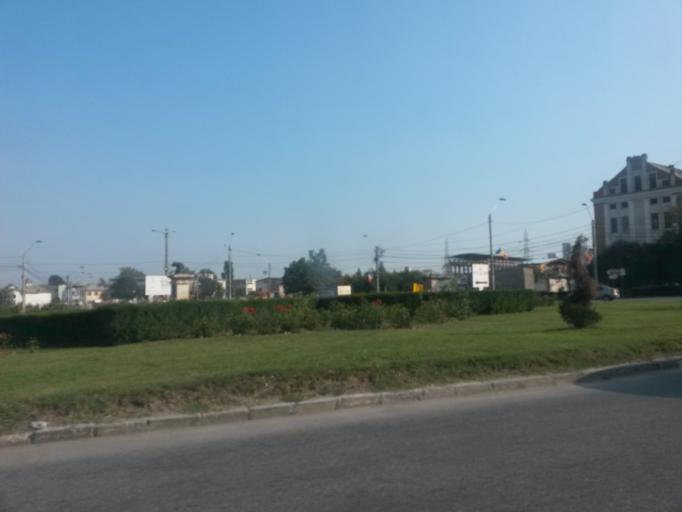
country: RO
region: Cluj
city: Turda
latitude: 46.5652
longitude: 23.7796
